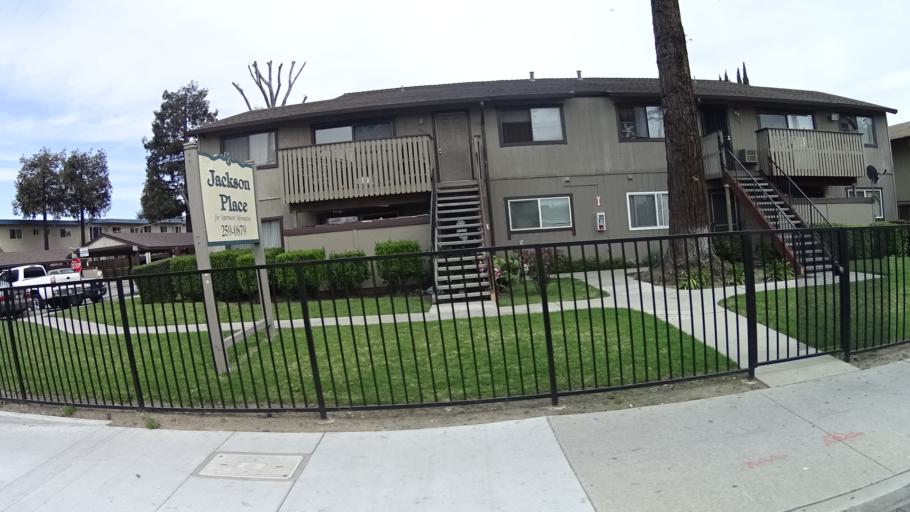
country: US
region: California
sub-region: Santa Clara County
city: Alum Rock
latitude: 37.3596
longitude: -121.8445
